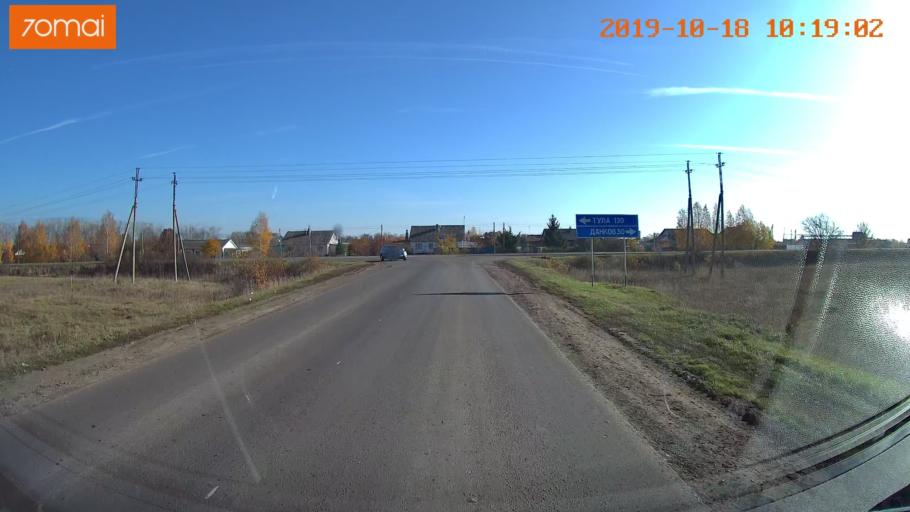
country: RU
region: Tula
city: Kurkino
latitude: 53.4182
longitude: 38.6447
